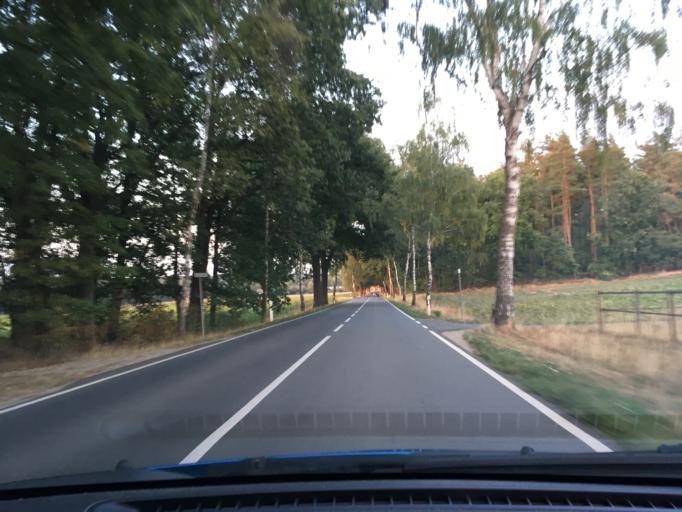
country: DE
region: Lower Saxony
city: Hitzacker
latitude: 53.1440
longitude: 10.9911
